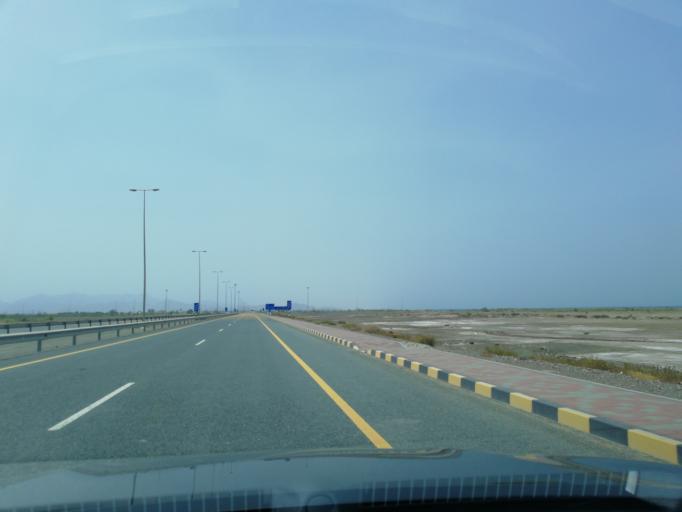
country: OM
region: Al Batinah
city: Shinas
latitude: 24.8604
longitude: 56.4153
